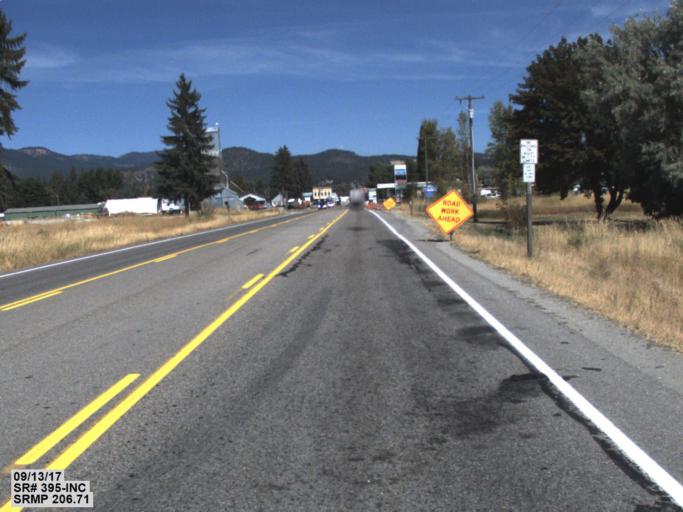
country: US
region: Washington
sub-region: Stevens County
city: Chewelah
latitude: 48.2701
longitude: -117.7153
